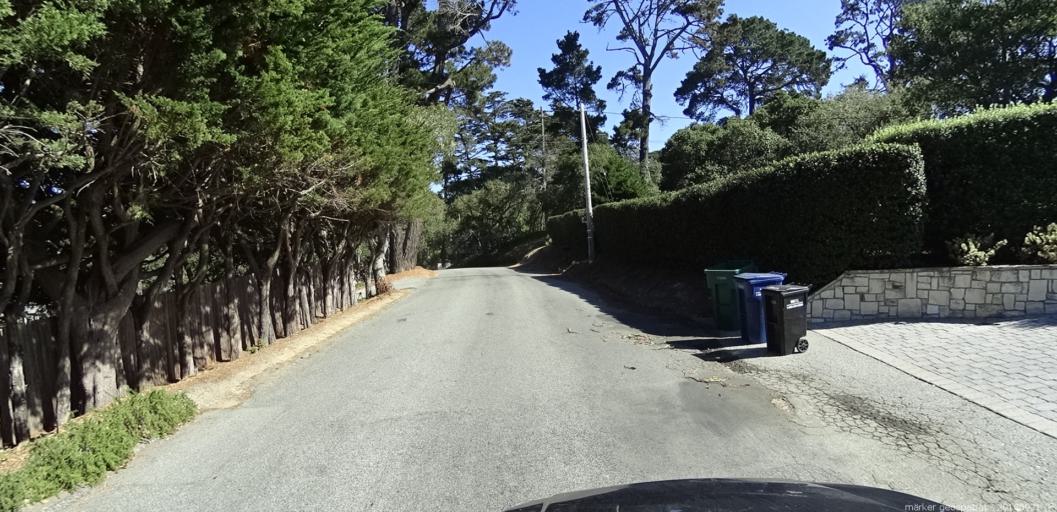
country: US
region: California
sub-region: Monterey County
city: Carmel-by-the-Sea
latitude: 36.5541
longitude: -121.9123
